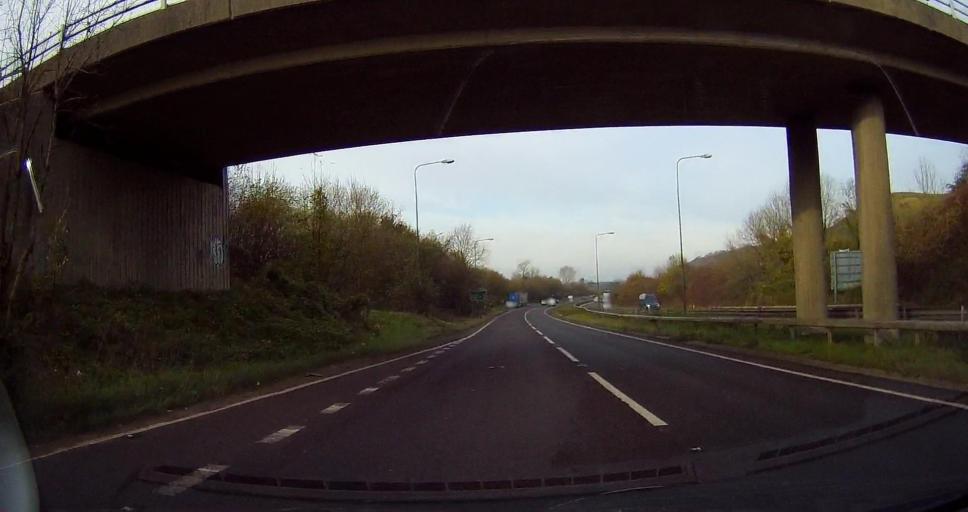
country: GB
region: England
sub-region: West Sussex
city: Hassocks
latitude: 50.9027
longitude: -0.1825
